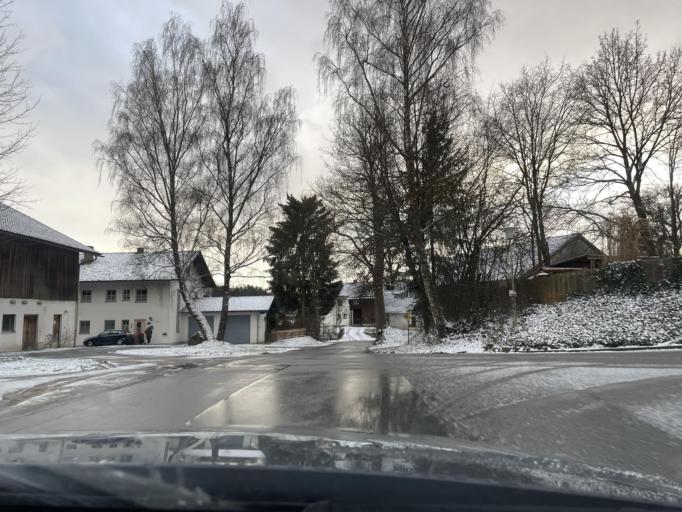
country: DE
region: Bavaria
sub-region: Lower Bavaria
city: Viechtach
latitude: 49.0962
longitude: 12.8704
